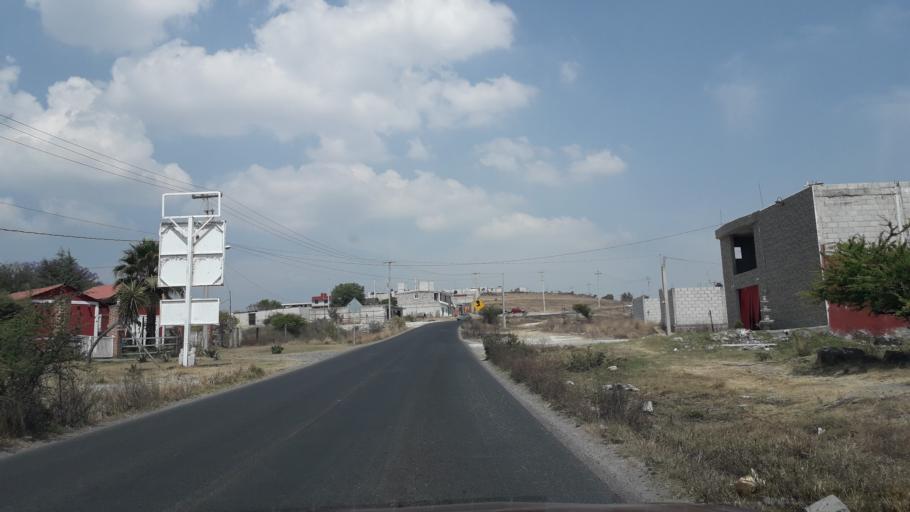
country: MX
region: Puebla
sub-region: Puebla
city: El Capulo (La Quebradora)
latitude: 18.9289
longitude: -98.2575
